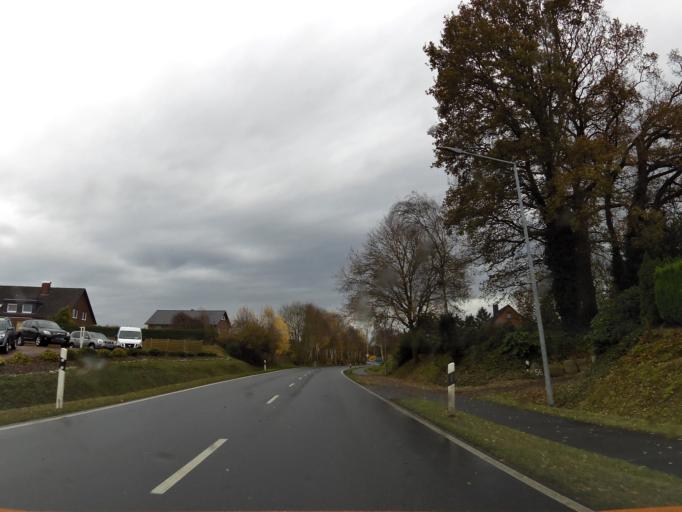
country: DE
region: Lower Saxony
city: Hude
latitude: 53.0991
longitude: 8.4883
